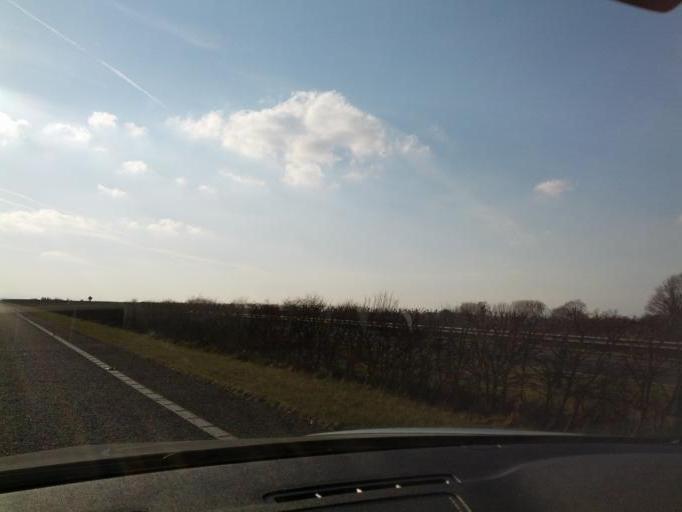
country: IE
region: Leinster
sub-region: Kildare
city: Cherryville
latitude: 53.1521
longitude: -6.9716
